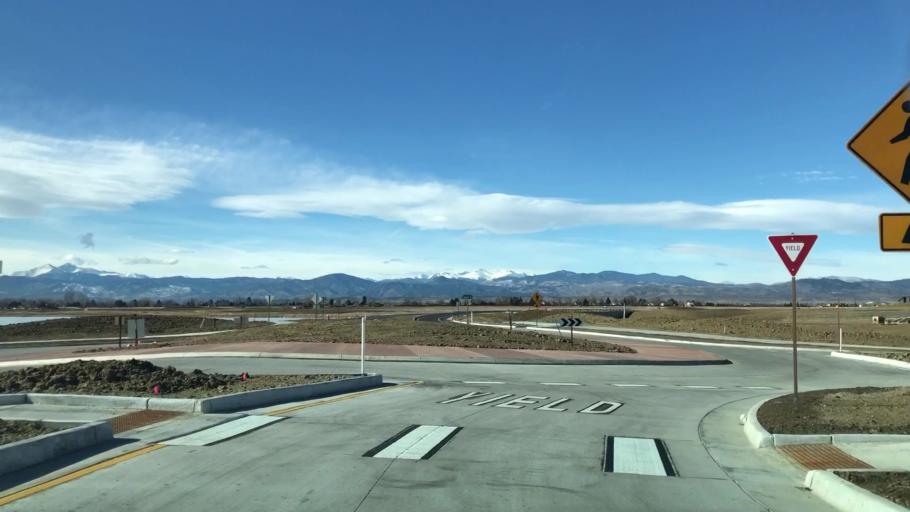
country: US
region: Colorado
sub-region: Larimer County
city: Loveland
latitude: 40.4266
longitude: -105.0049
